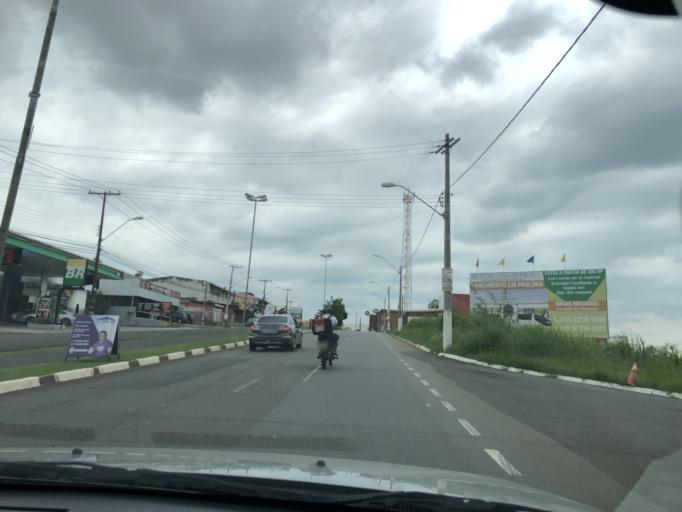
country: BR
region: Sao Paulo
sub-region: Paulinia
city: Paulinia
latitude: -22.7506
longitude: -47.1697
